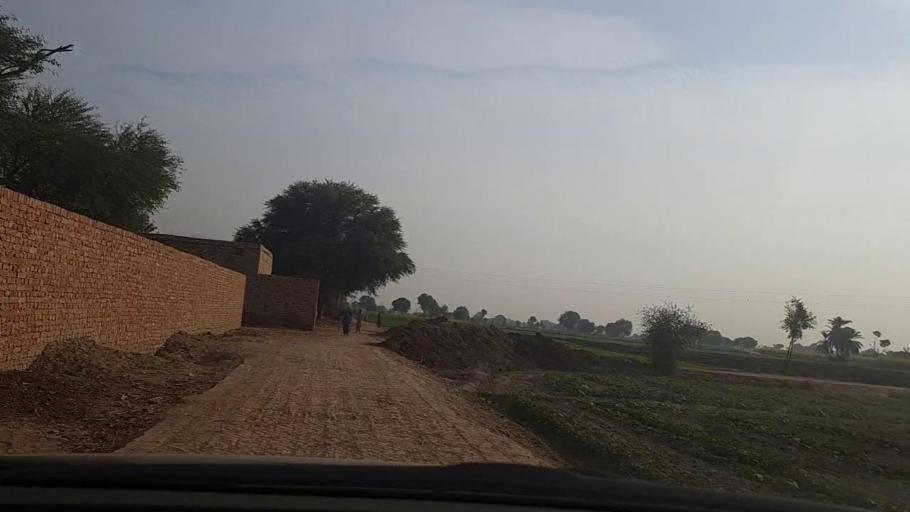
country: PK
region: Sindh
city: Daulatpur
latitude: 26.3305
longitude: 68.0552
